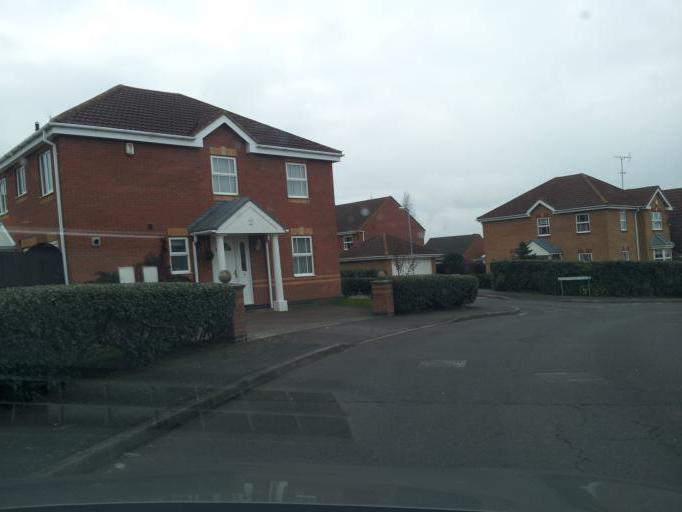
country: GB
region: England
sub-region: Lincolnshire
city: Great Gonerby
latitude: 52.9182
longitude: -0.6621
